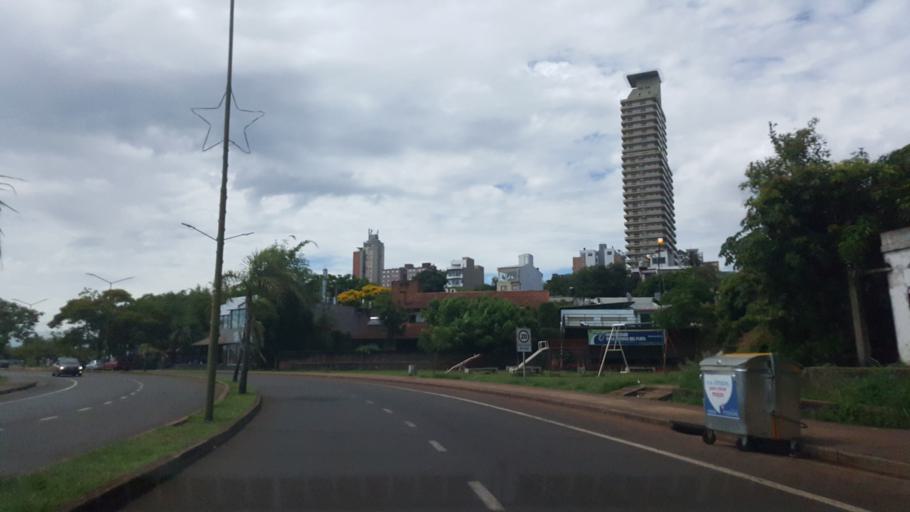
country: AR
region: Misiones
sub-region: Departamento de Capital
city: Posadas
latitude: -27.3600
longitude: -55.8890
